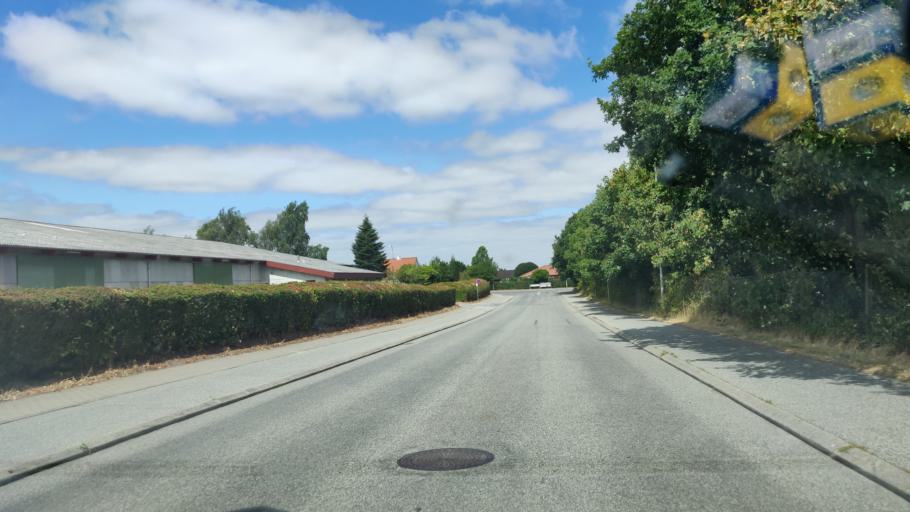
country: DK
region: South Denmark
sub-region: Fredericia Kommune
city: Taulov
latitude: 55.5356
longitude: 9.6203
